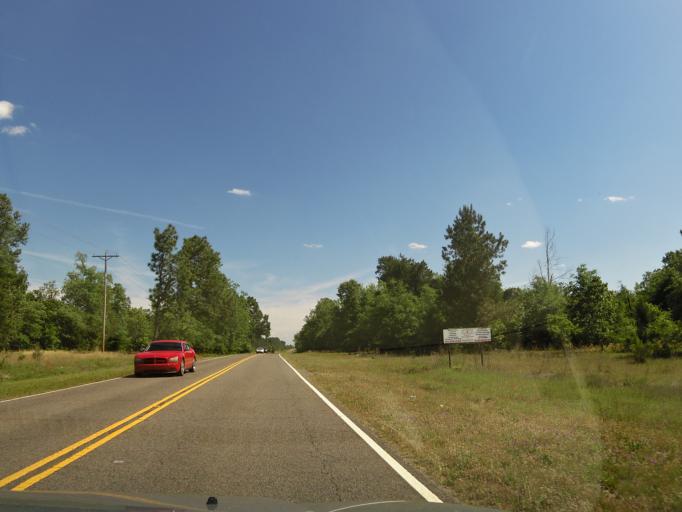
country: US
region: South Carolina
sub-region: Barnwell County
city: Williston
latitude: 33.4537
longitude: -81.4938
